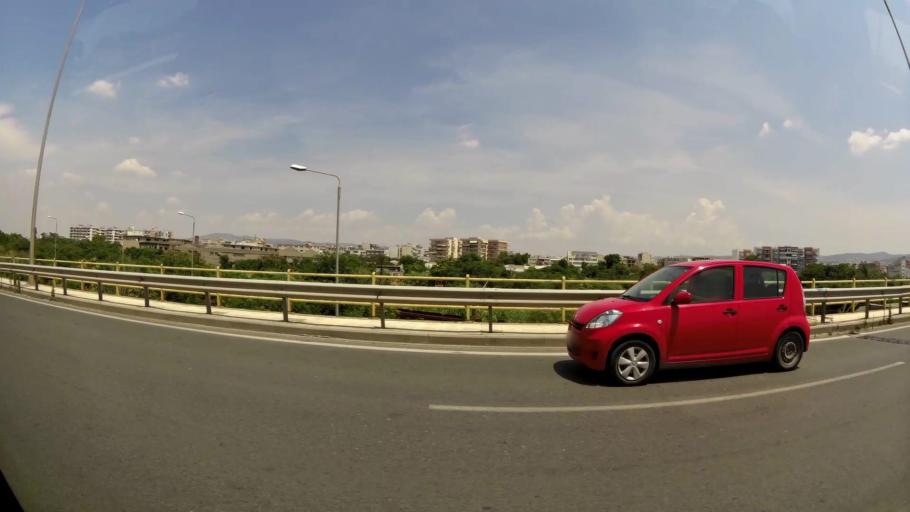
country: GR
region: Central Macedonia
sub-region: Nomos Thessalonikis
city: Menemeni
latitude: 40.6489
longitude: 22.9103
